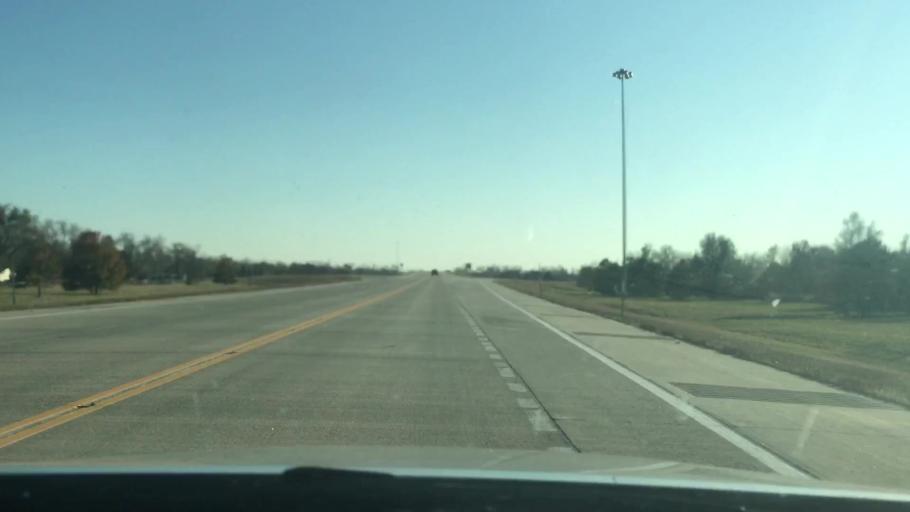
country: US
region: Kansas
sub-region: Reno County
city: Hutchinson
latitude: 38.0622
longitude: -97.9859
